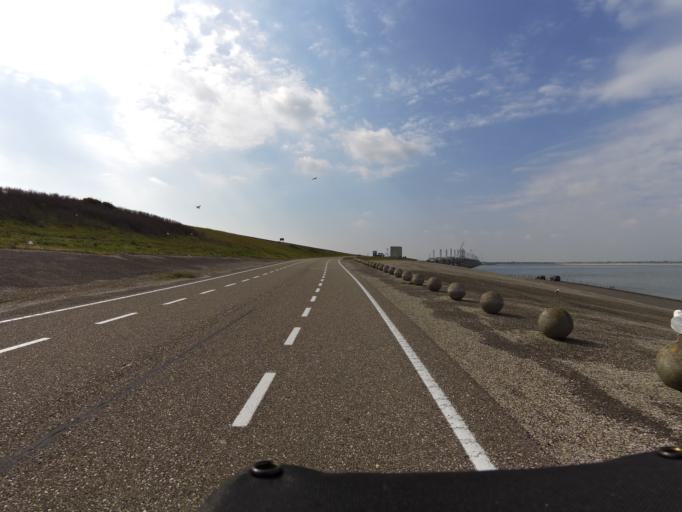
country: NL
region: Zeeland
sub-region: Gemeente Noord-Beveland
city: Kamperland
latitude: 51.6167
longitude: 3.6836
